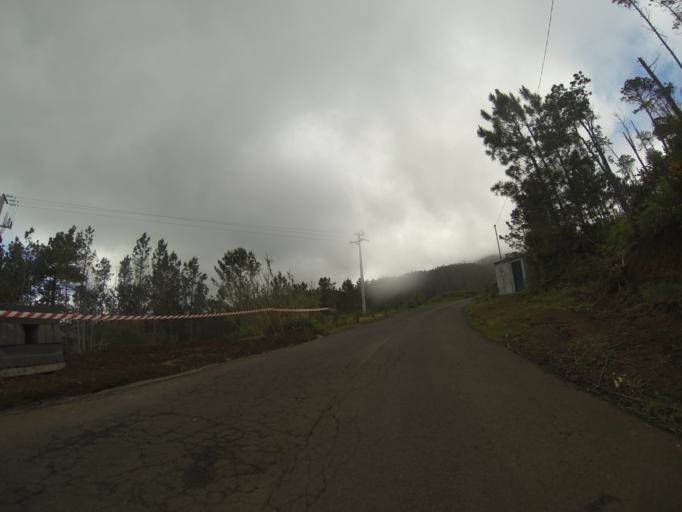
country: PT
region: Madeira
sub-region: Calheta
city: Estreito da Calheta
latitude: 32.7626
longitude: -17.1977
